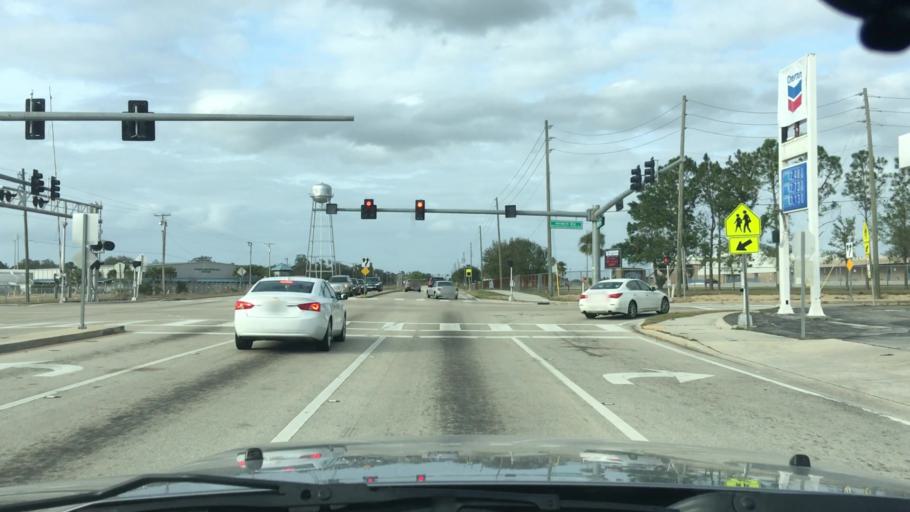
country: US
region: Florida
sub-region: Highlands County
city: Sebring
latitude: 27.4854
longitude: -81.4334
